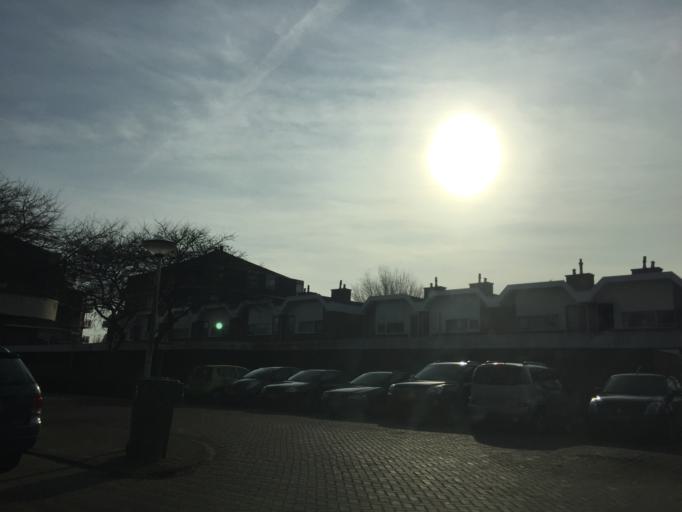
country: NL
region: South Holland
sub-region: Gemeente Leiden
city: Leiden
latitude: 52.1811
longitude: 4.5039
